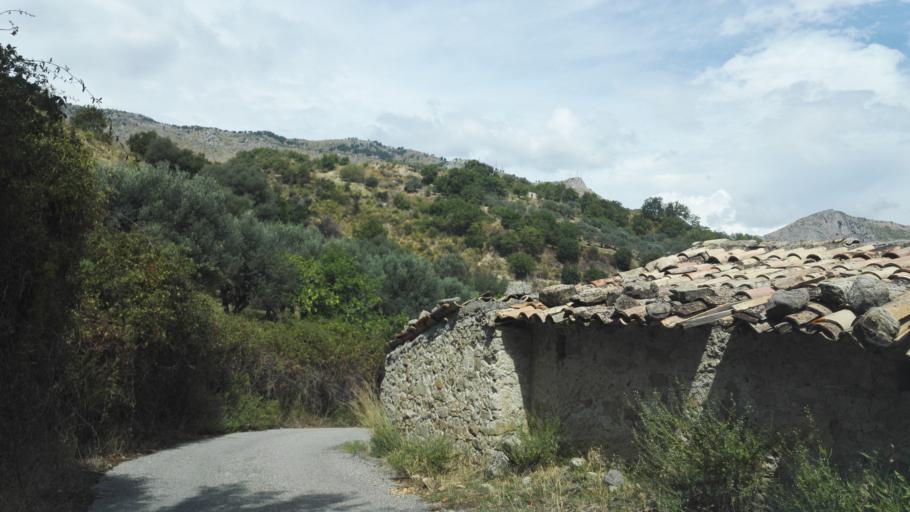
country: IT
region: Calabria
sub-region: Provincia di Reggio Calabria
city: Stilo
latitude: 38.4547
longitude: 16.4627
